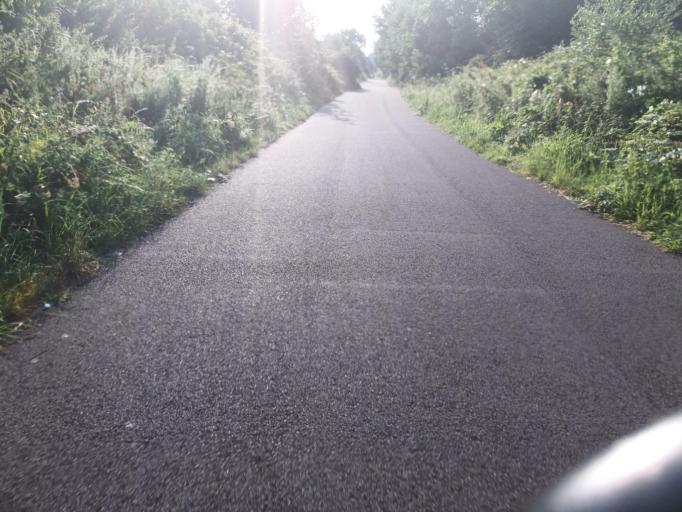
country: GB
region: Northern Ireland
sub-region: Castlereagh District
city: Dundonald
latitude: 54.5909
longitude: -5.8351
